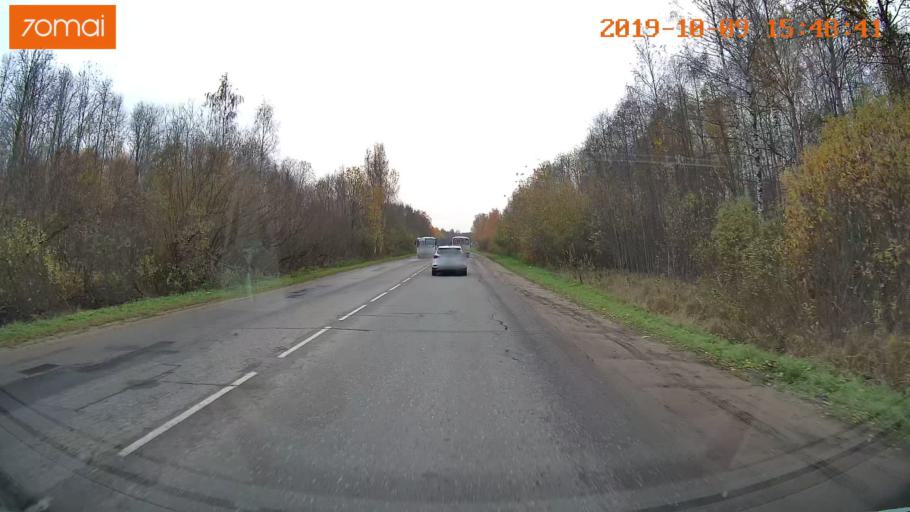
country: RU
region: Kostroma
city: Oktyabr'skiy
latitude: 57.8104
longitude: 41.0123
